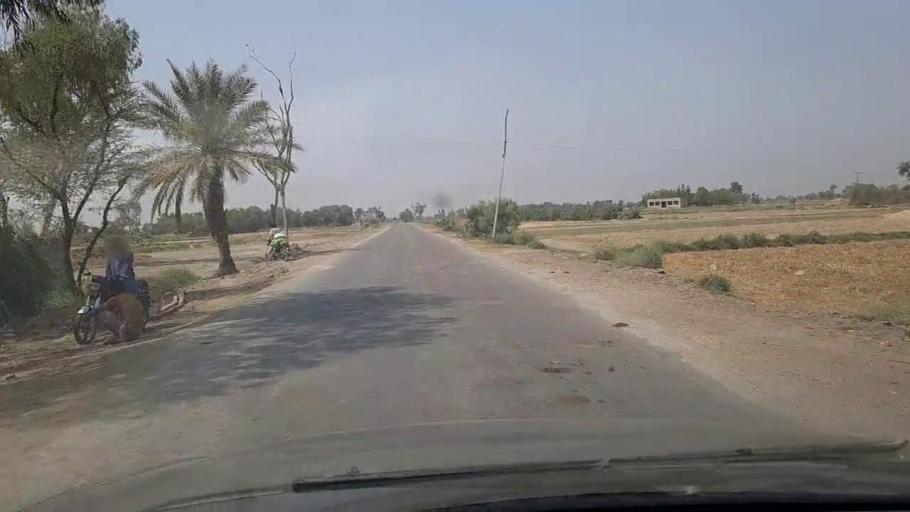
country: PK
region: Sindh
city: Khanpur
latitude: 27.8846
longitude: 69.4732
